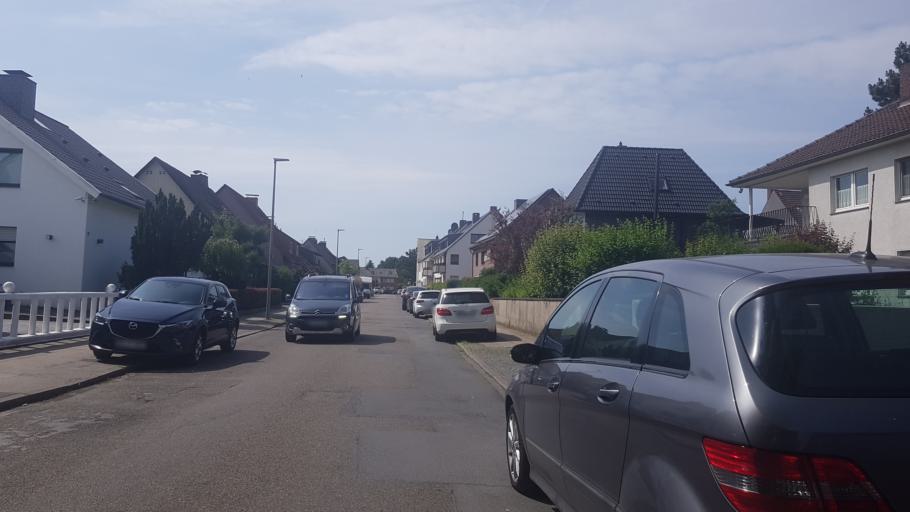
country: DE
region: North Rhine-Westphalia
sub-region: Regierungsbezirk Dusseldorf
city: Oberhausen
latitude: 51.4619
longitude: 6.8714
